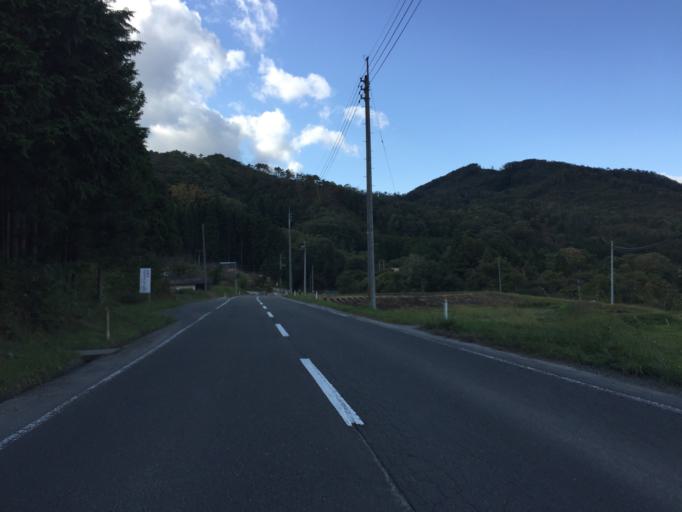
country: JP
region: Miyagi
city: Marumori
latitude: 37.8376
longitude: 140.8316
